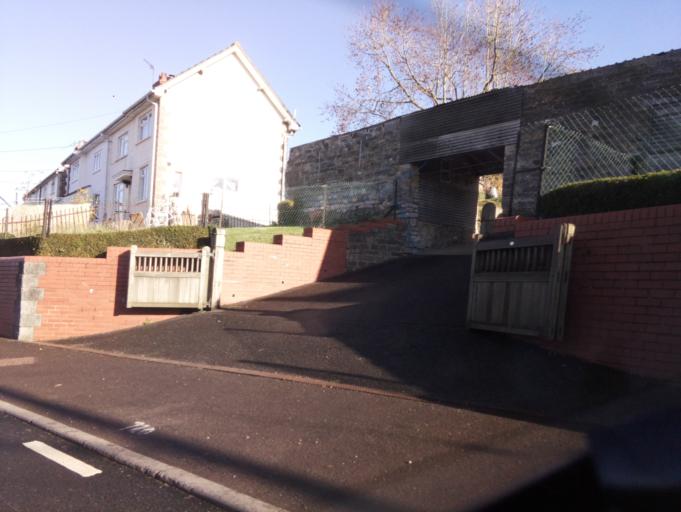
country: GB
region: England
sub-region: Somerset
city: Langport
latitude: 51.0614
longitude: -2.8579
